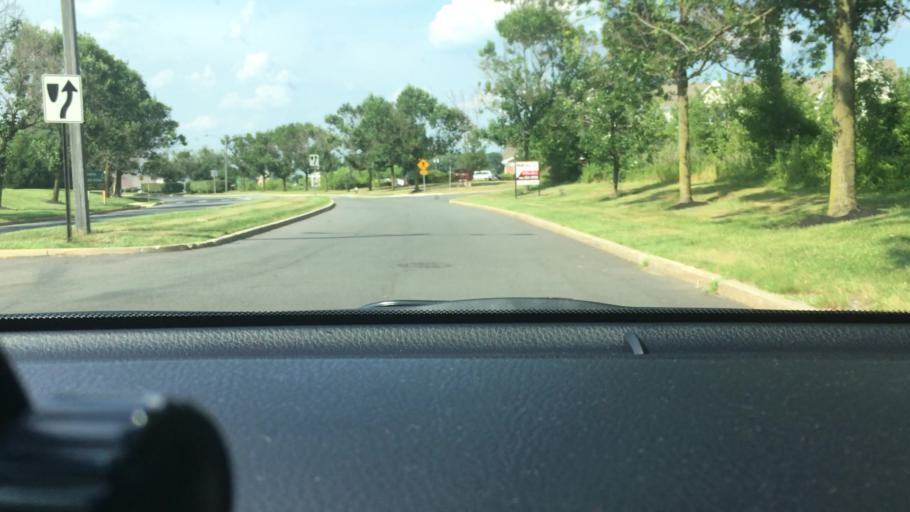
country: US
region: New Jersey
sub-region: Burlington County
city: Mount Laurel
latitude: 39.9663
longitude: -74.9032
